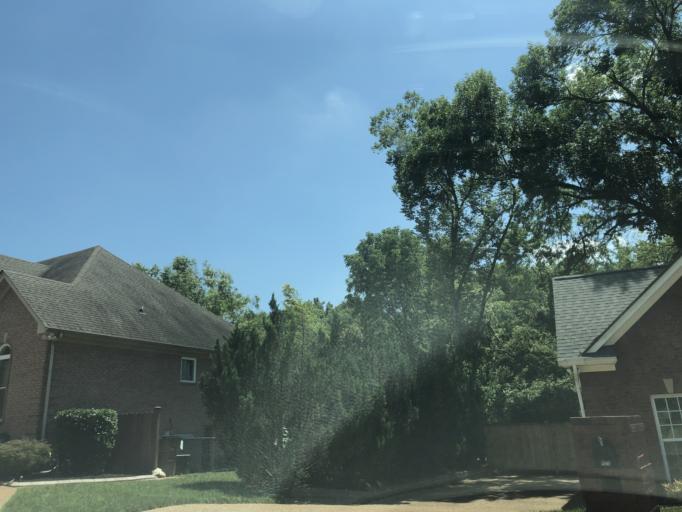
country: US
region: Tennessee
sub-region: Davidson County
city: Lakewood
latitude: 36.1776
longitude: -86.6475
